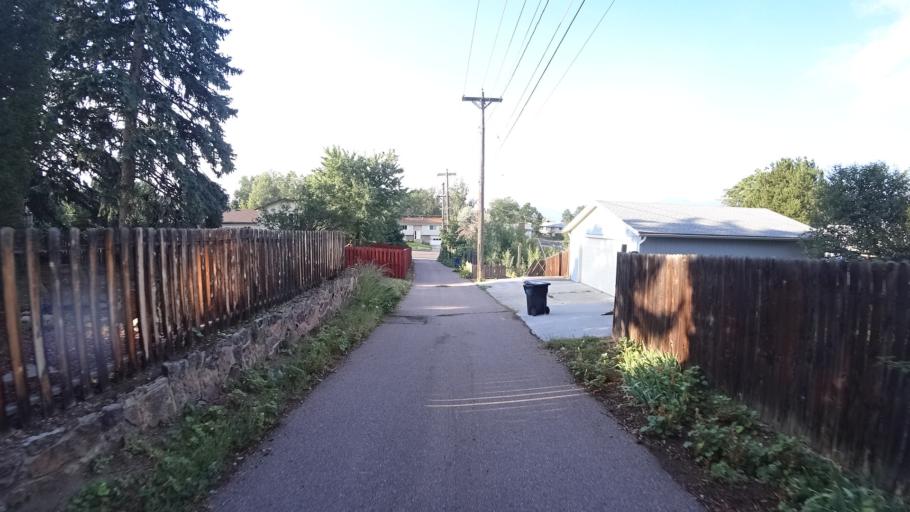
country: US
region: Colorado
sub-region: El Paso County
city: Colorado Springs
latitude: 38.8902
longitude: -104.8069
